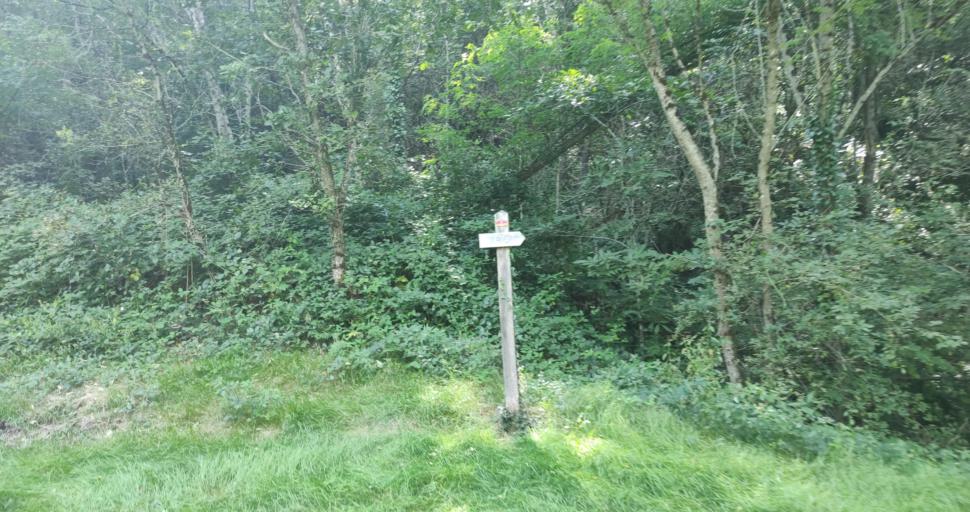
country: FR
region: Midi-Pyrenees
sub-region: Departement de l'Aveyron
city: Cransac
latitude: 44.5370
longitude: 2.2731
